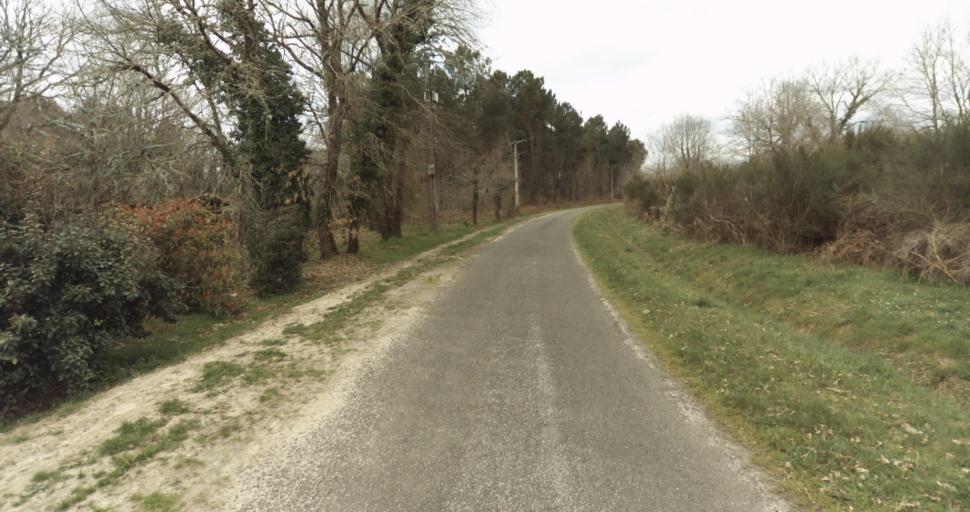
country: FR
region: Aquitaine
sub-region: Departement des Landes
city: Roquefort
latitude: 44.0748
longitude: -0.3969
